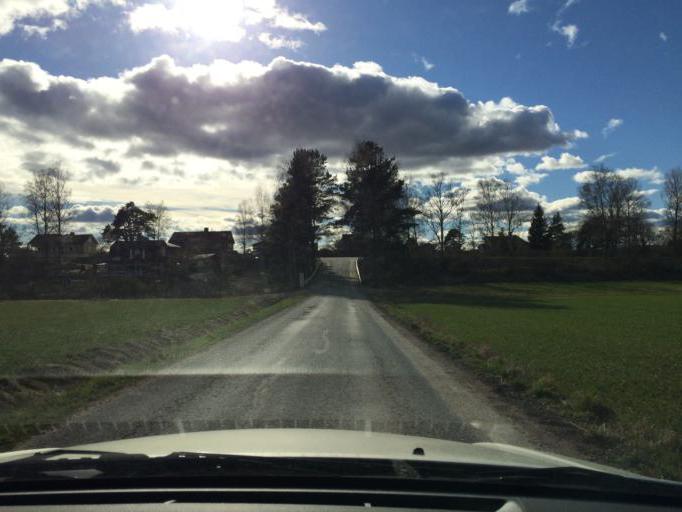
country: SE
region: Soedermanland
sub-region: Eskilstuna Kommun
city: Kvicksund
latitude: 59.4330
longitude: 16.3415
